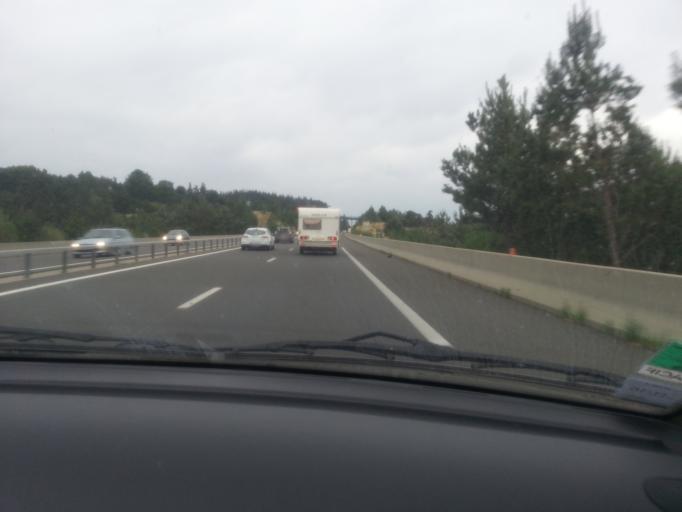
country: FR
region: Languedoc-Roussillon
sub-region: Departement de la Lozere
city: Marvejols
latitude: 44.5982
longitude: 3.2545
